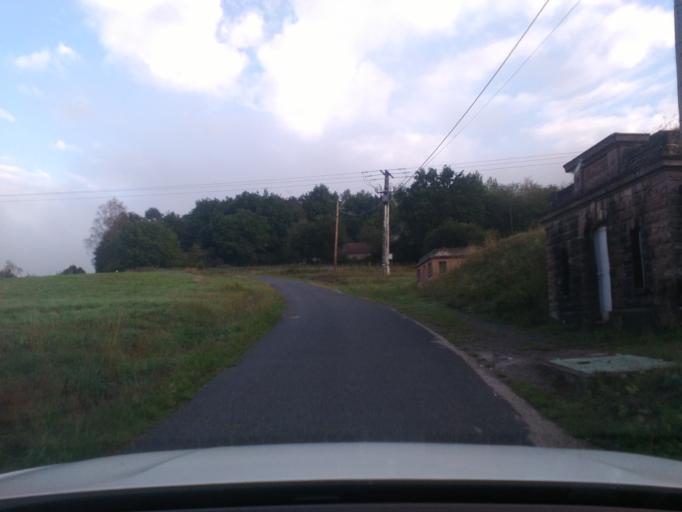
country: FR
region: Lorraine
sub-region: Departement des Vosges
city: Moyenmoutier
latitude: 48.3801
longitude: 6.9076
